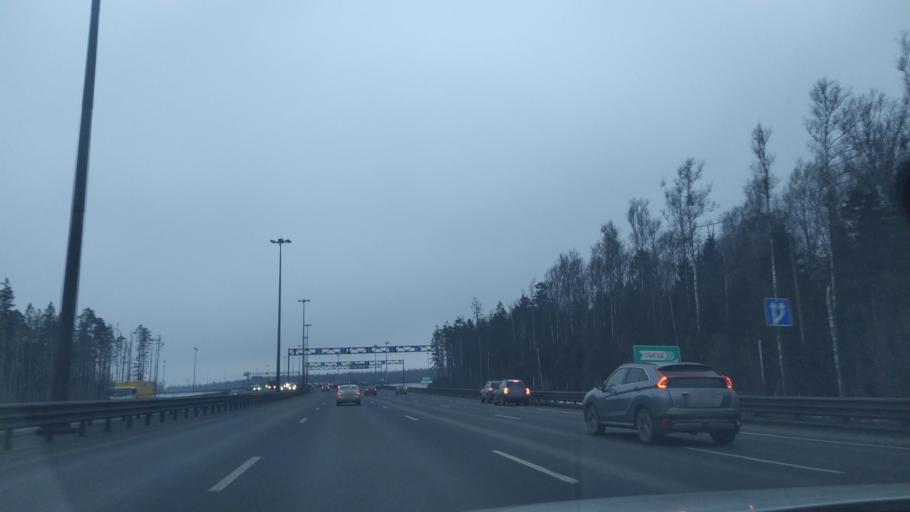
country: RU
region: Leningrad
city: Yanino Vtoroye
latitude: 59.9511
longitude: 30.5450
